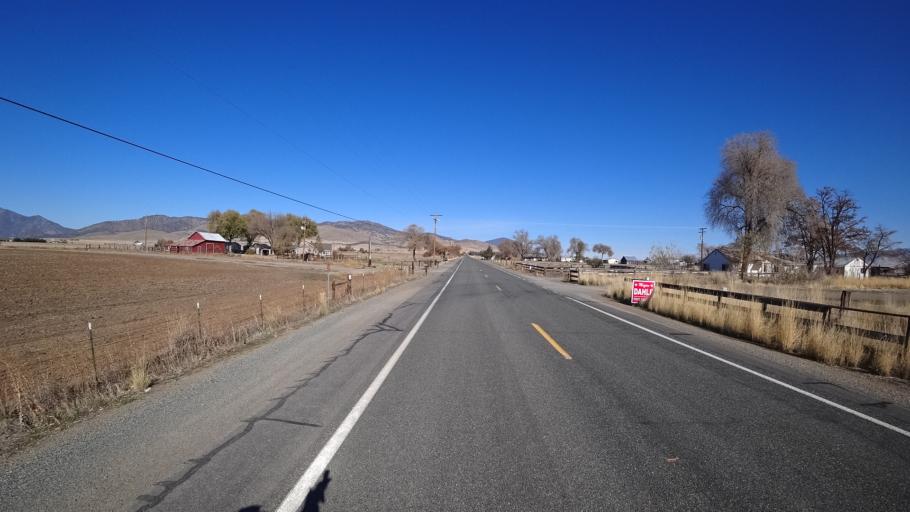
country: US
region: California
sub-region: Siskiyou County
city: Montague
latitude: 41.7560
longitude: -122.5247
